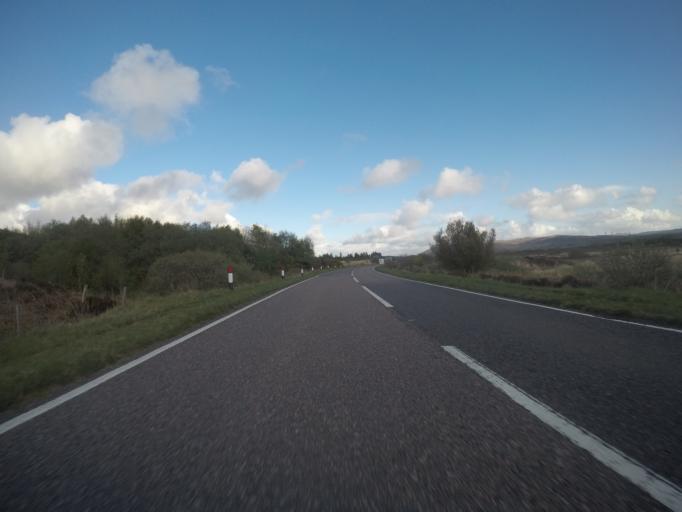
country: GB
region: Scotland
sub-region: Highland
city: Portree
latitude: 57.4576
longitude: -6.2737
